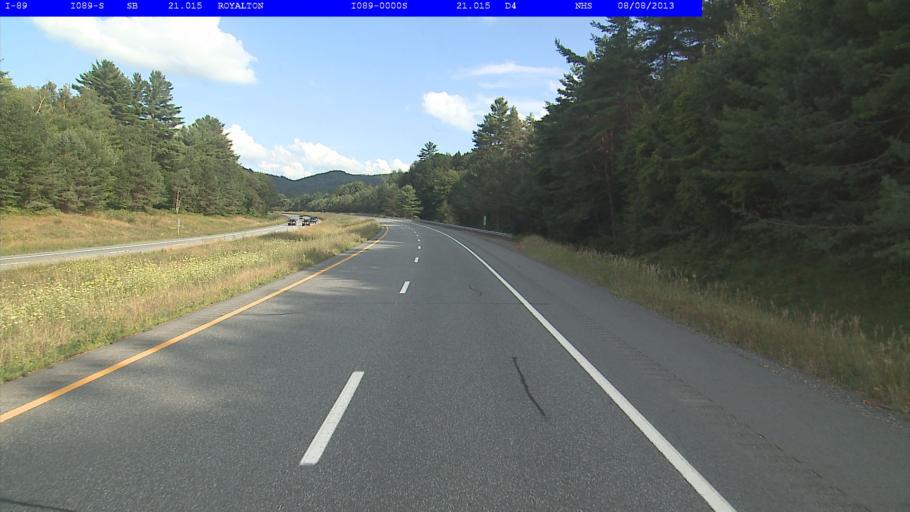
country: US
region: Vermont
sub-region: Orange County
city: Randolph
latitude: 43.8141
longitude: -72.5661
